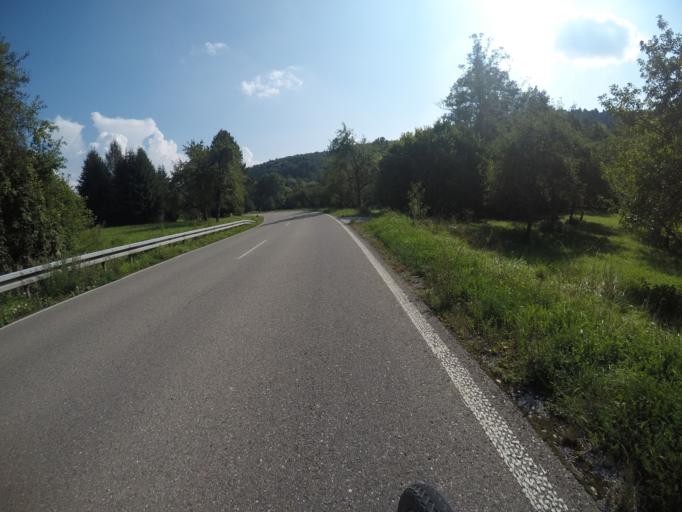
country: DE
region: Baden-Wuerttemberg
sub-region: Regierungsbezirk Stuttgart
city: Filderstadt
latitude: 48.6311
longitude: 9.1923
